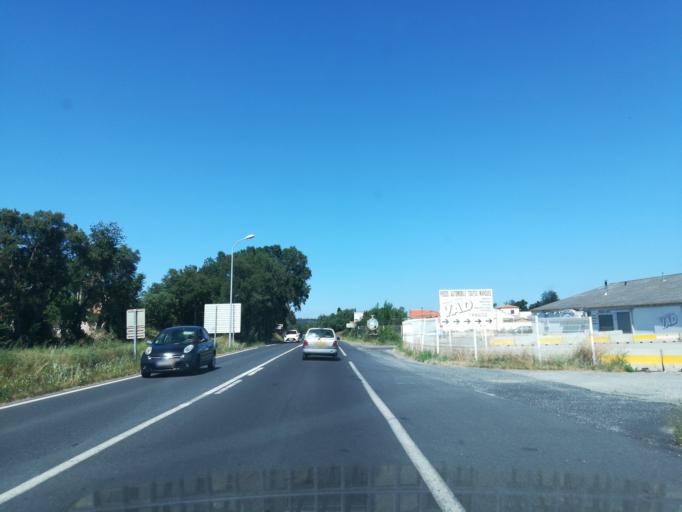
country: FR
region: Languedoc-Roussillon
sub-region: Departement des Pyrenees-Orientales
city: Sant Joan de Pladecorts
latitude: 42.5153
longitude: 2.7880
